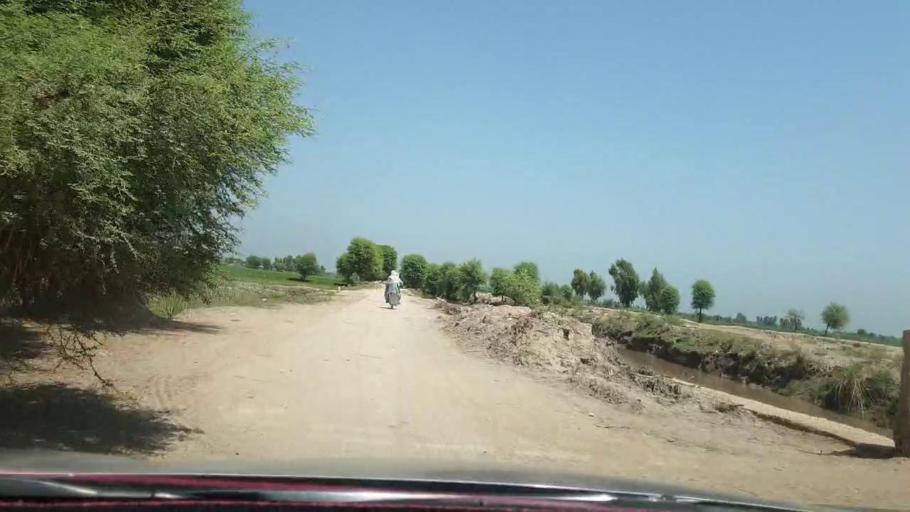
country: PK
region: Sindh
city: Warah
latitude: 27.5202
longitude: 67.8155
